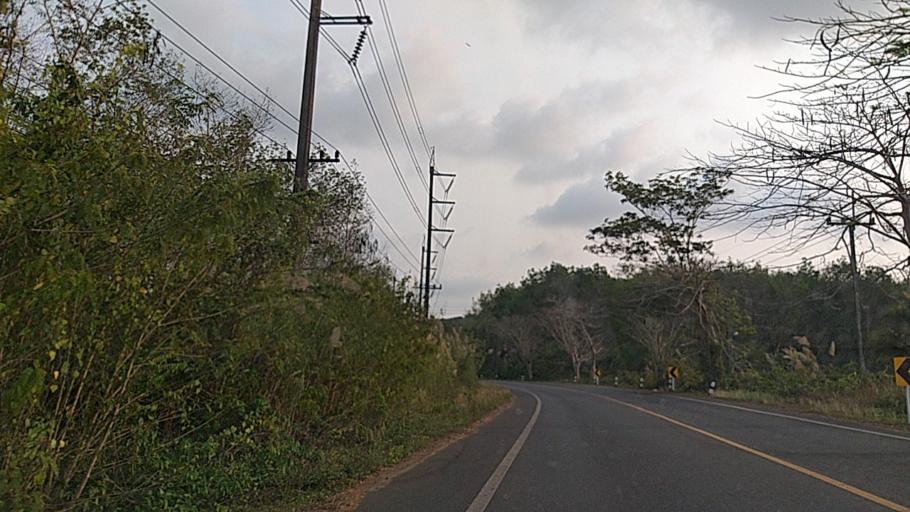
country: TH
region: Trat
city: Laem Ngop
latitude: 12.2760
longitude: 102.3058
